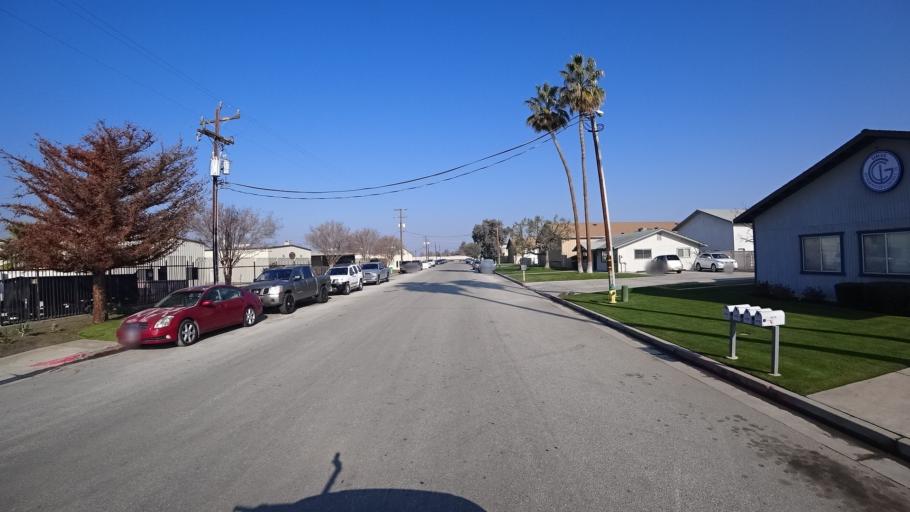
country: US
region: California
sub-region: Kern County
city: Greenacres
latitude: 35.3741
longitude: -119.1077
